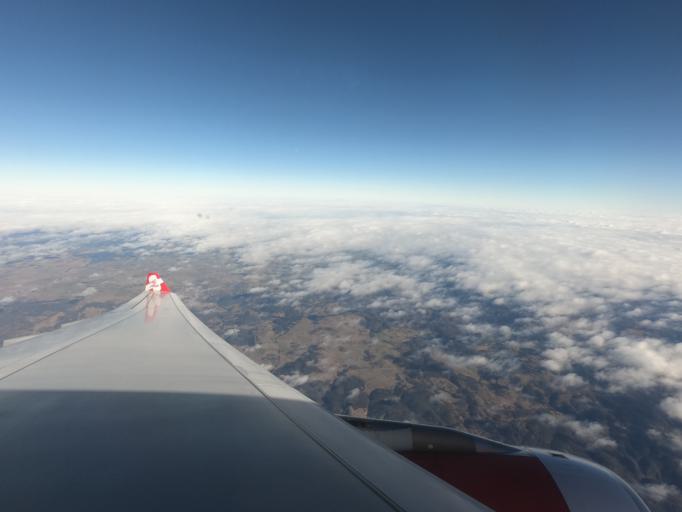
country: AU
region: New South Wales
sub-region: Wingecarribee
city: Bundanoon
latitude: -34.4436
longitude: 150.0303
